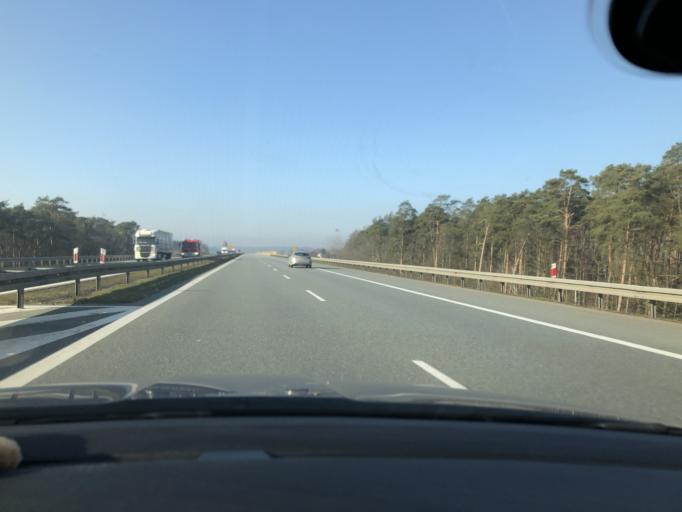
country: PL
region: Greater Poland Voivodeship
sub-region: Powiat poznanski
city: Dopiewo
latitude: 52.3495
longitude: 16.6623
